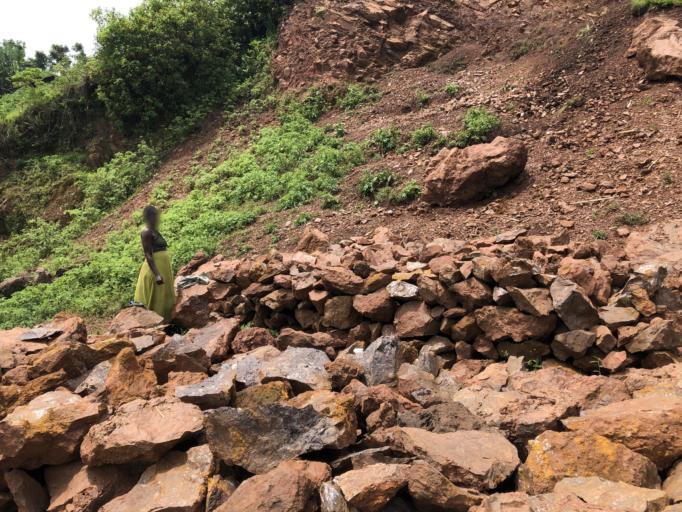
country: CD
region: Nord Kivu
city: Sake
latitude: -1.7172
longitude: 29.0186
